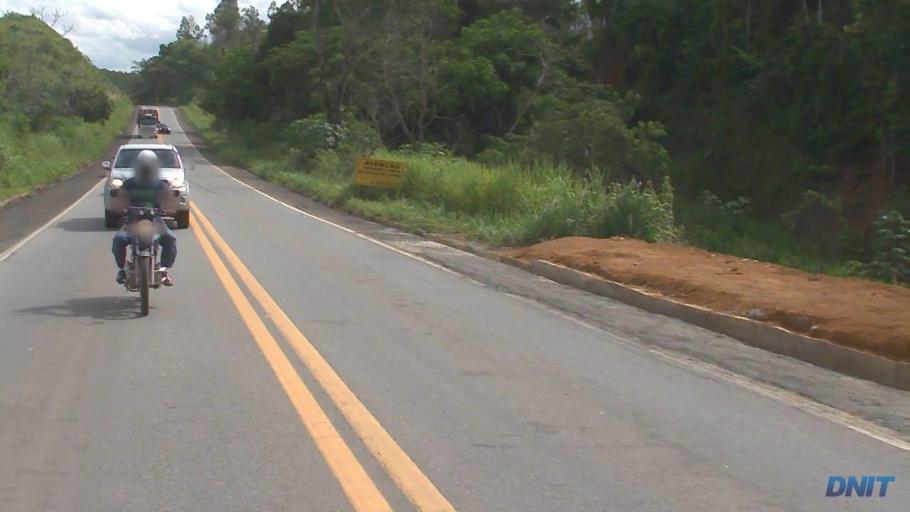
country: BR
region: Minas Gerais
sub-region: Ipaba
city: Ipaba
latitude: -19.3399
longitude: -42.4286
